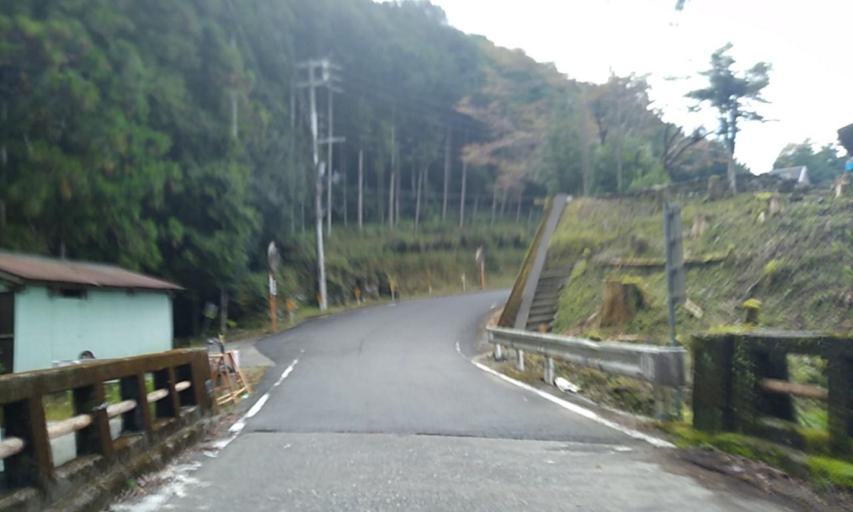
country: JP
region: Wakayama
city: Shingu
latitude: 33.9325
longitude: 135.9793
